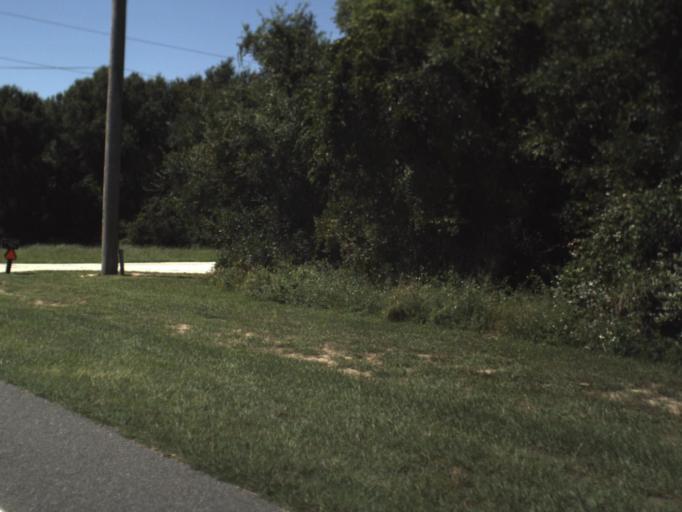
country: US
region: Florida
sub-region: Polk County
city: Dundee
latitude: 27.9962
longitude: -81.5950
